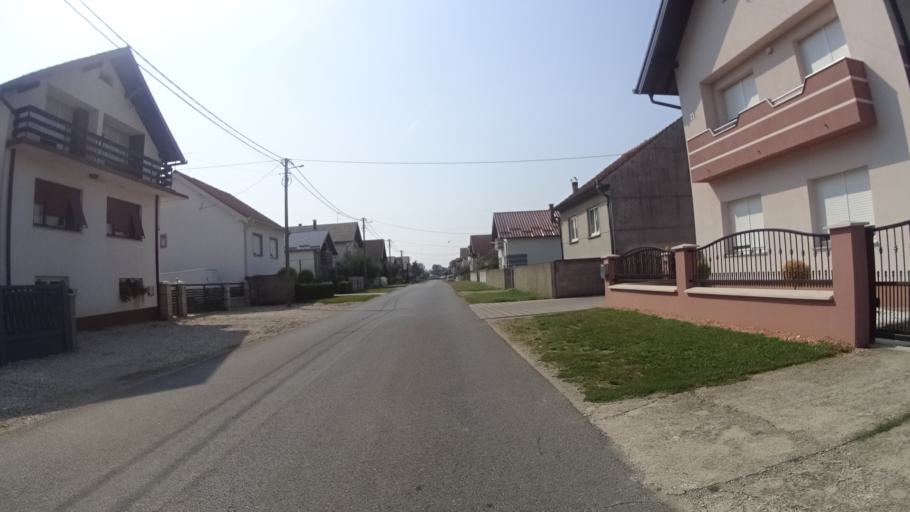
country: HR
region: Medimurska
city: Belica
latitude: 46.3990
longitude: 16.5089
